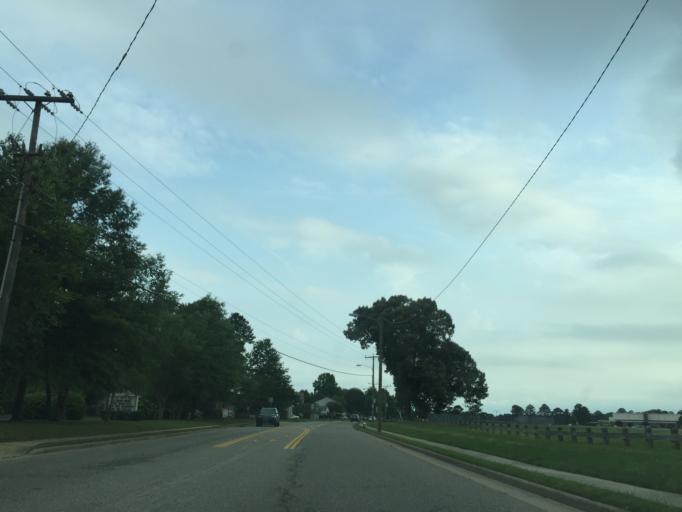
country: US
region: Virginia
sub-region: York County
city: Yorktown
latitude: 37.0997
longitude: -76.5266
